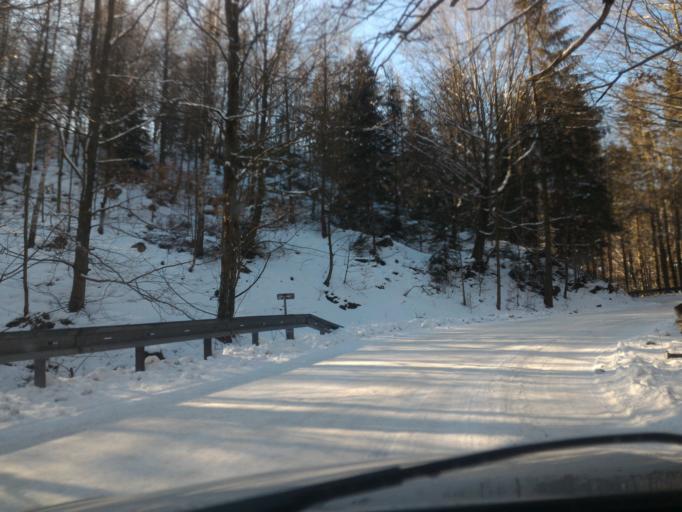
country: CZ
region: Liberecky
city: Nove Mesto pod Smrkem
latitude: 50.8647
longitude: 15.2517
